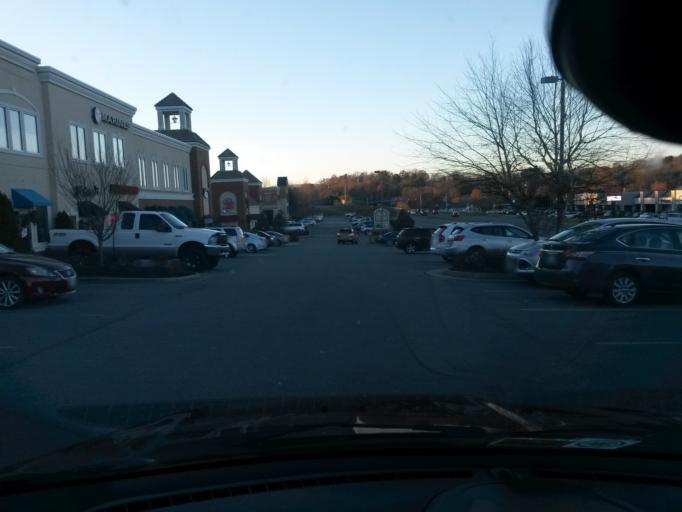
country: US
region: Virginia
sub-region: Roanoke County
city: Cave Spring
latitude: 37.2254
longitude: -79.9974
